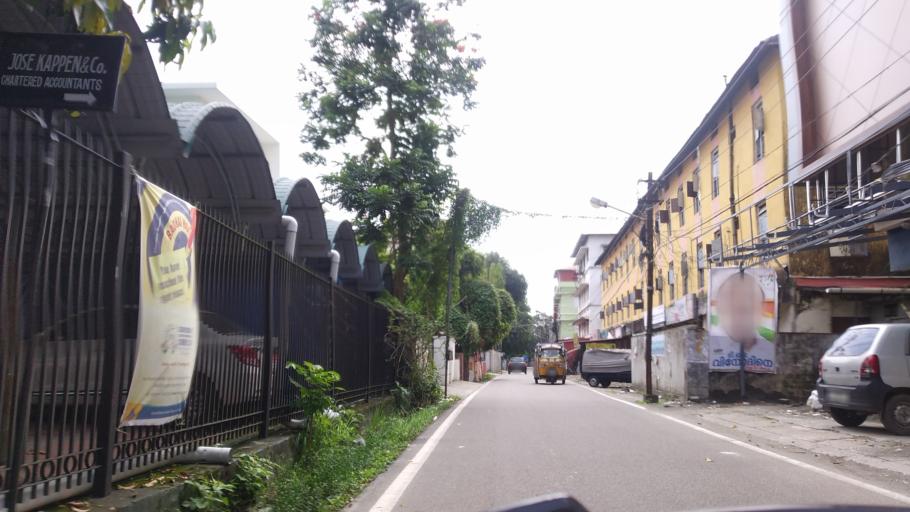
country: IN
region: Kerala
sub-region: Ernakulam
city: Cochin
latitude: 9.9869
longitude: 76.2794
